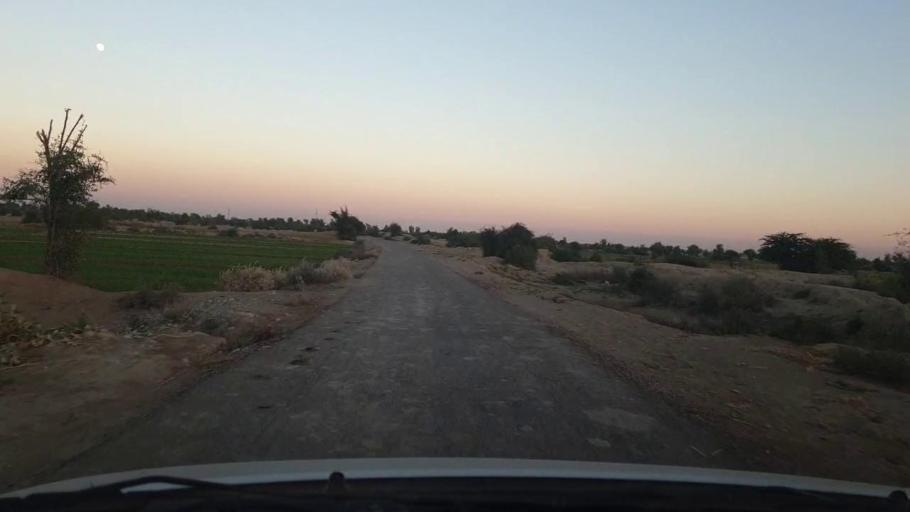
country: PK
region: Sindh
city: Johi
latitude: 26.8293
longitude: 67.4570
